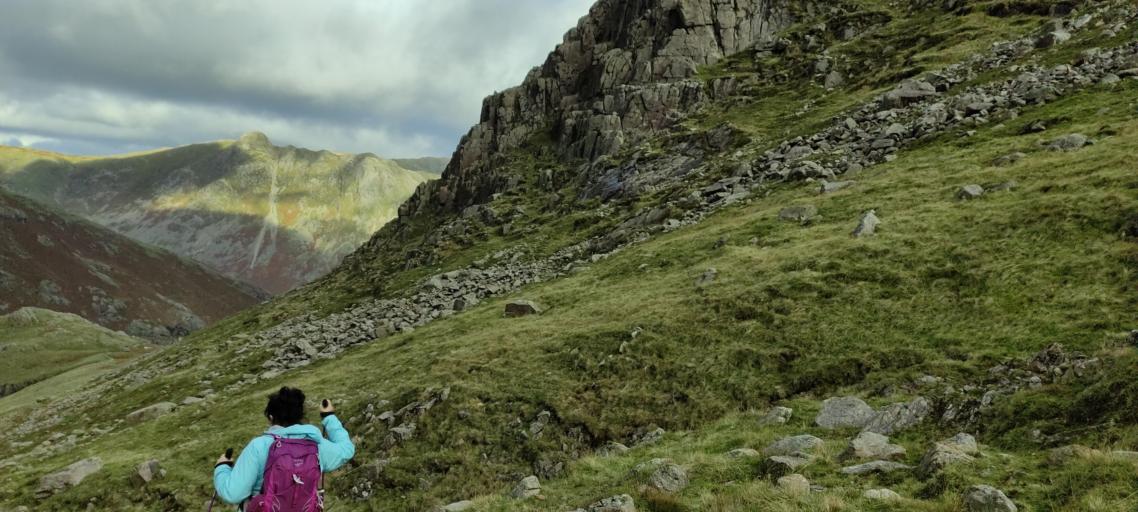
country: GB
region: England
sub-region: Cumbria
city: Ambleside
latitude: 54.4275
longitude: -3.1331
